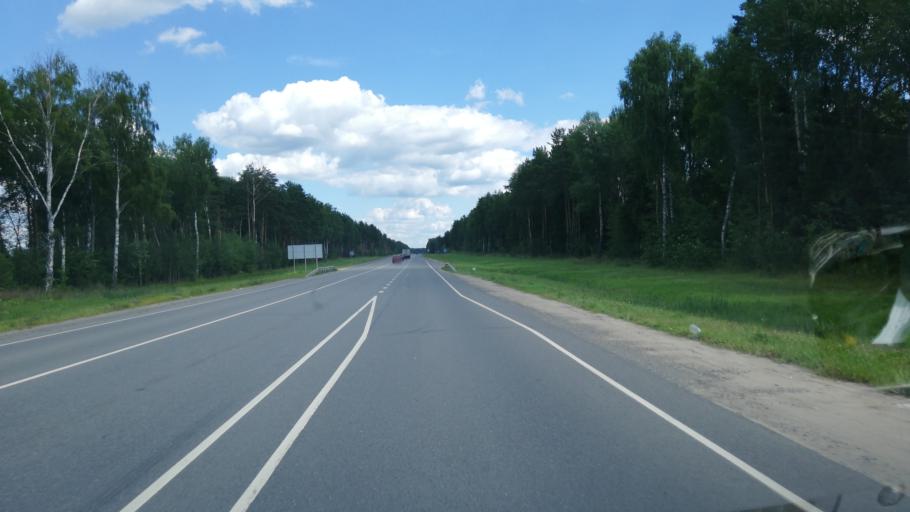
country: RU
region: Jaroslavl
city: Levashevo
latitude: 57.6396
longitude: 40.4659
